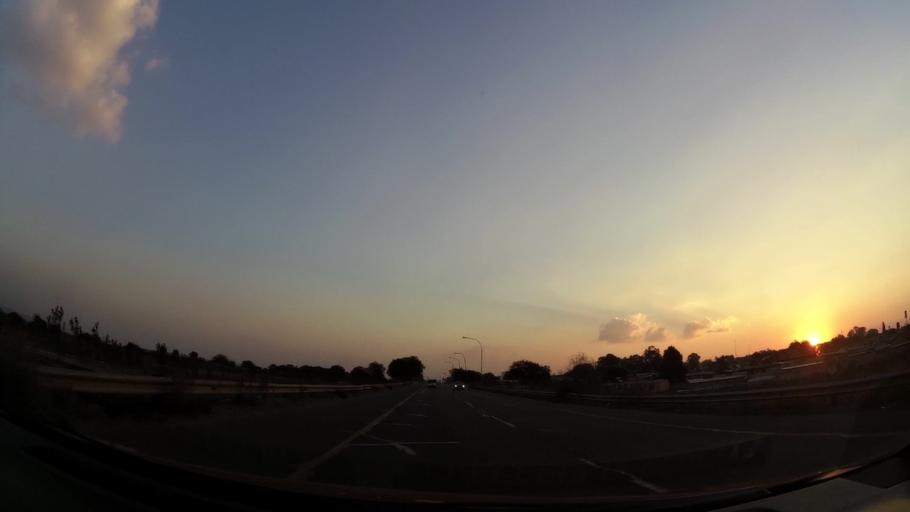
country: ZA
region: Gauteng
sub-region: City of Johannesburg Metropolitan Municipality
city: Soweto
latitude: -26.2908
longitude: 27.8835
